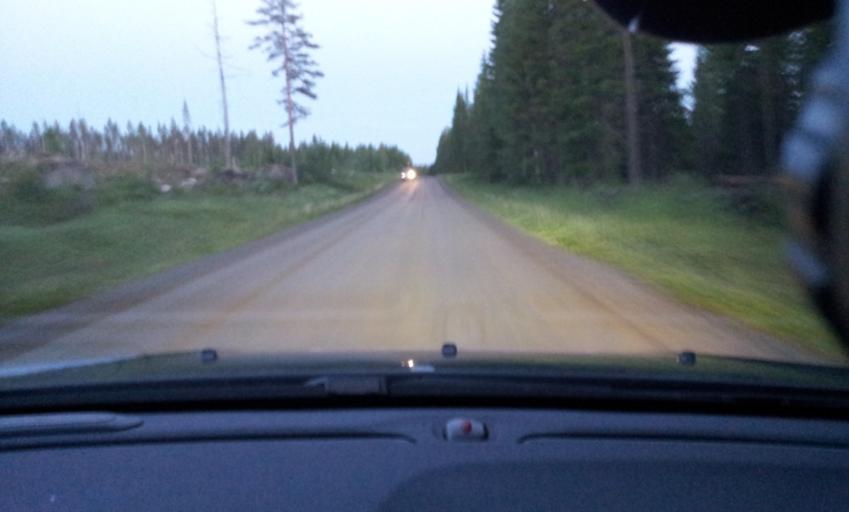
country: SE
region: Jaemtland
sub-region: Braecke Kommun
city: Braecke
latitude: 62.7457
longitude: 15.6417
